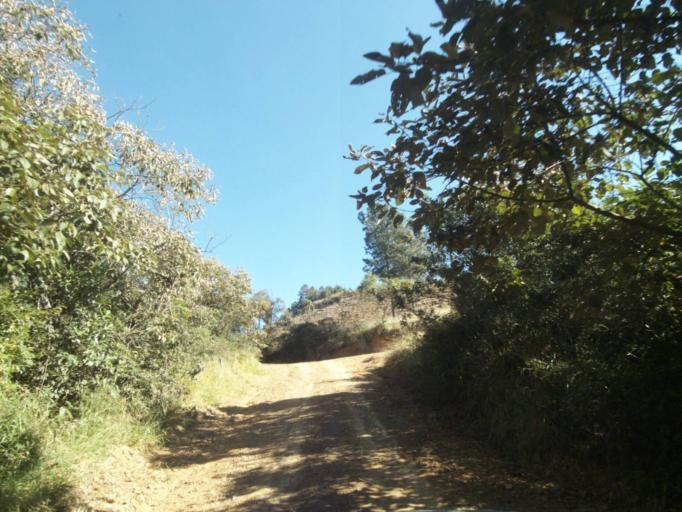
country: BR
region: Parana
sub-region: Tibagi
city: Tibagi
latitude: -24.5772
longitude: -50.4796
